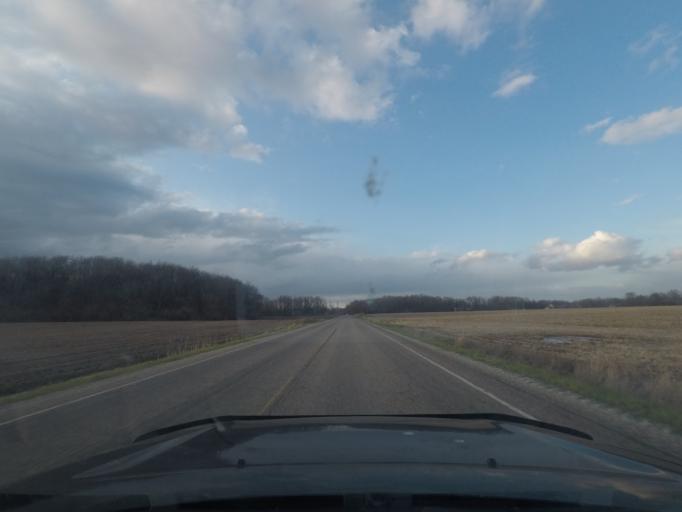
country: US
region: Indiana
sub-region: LaPorte County
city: LaPorte
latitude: 41.5426
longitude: -86.7403
